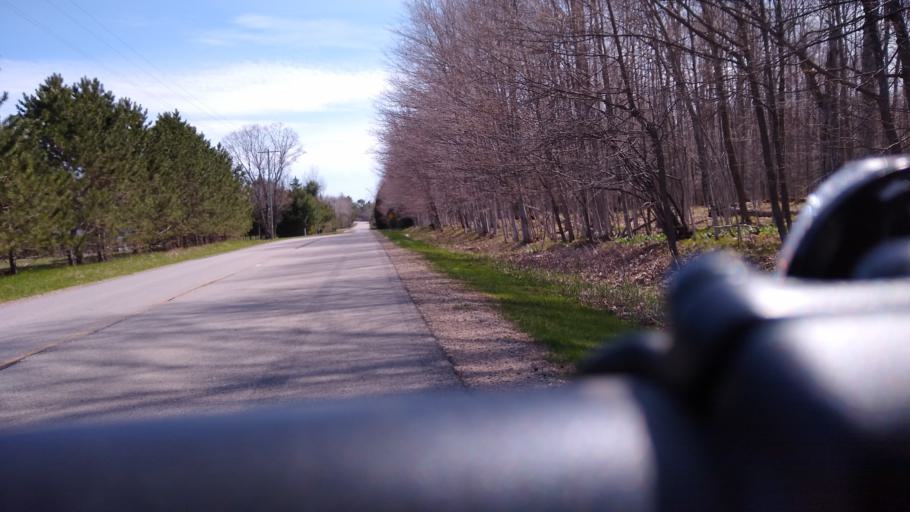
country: US
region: Michigan
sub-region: Delta County
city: Escanaba
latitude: 45.6934
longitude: -87.1526
